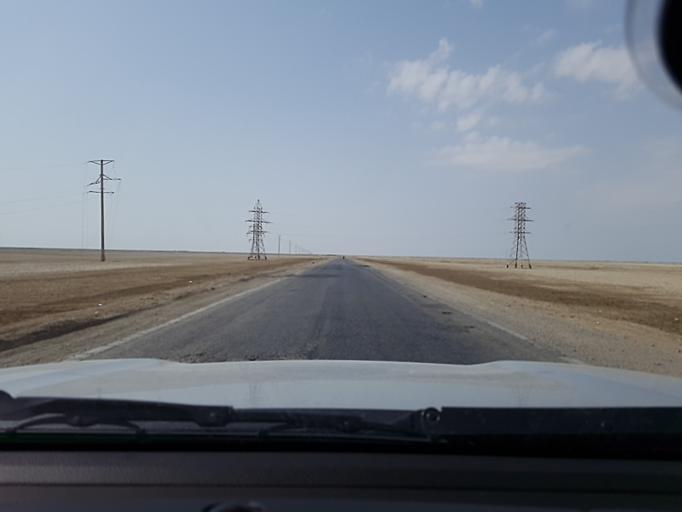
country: TM
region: Balkan
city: Gumdag
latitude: 39.0554
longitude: 54.5842
